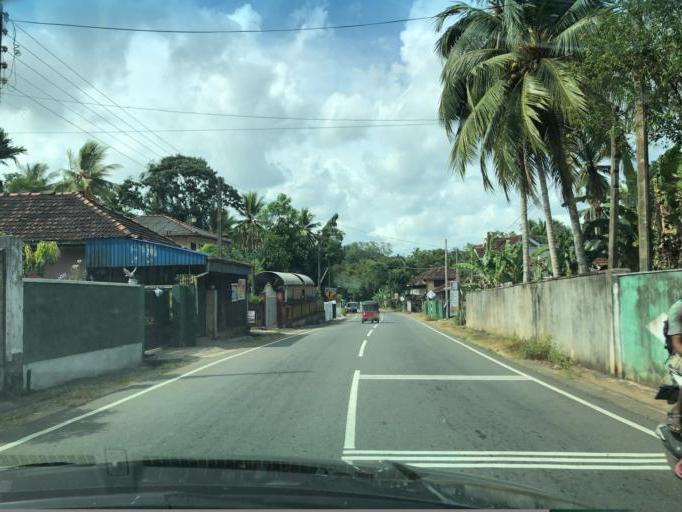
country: LK
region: Western
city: Horana South
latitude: 6.6456
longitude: 80.0766
